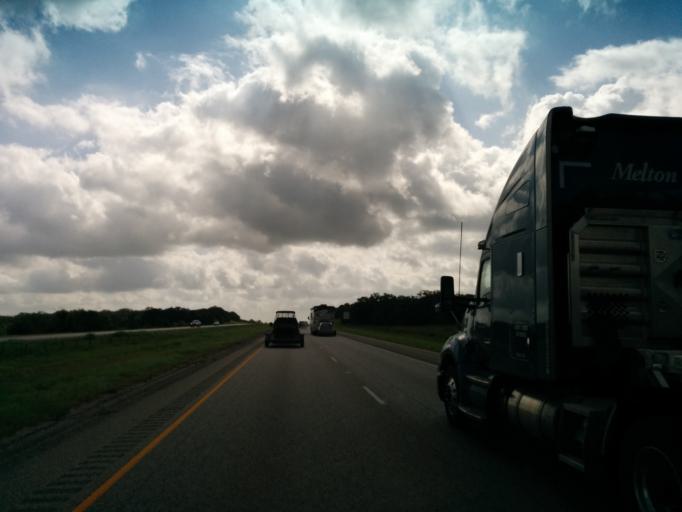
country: US
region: Texas
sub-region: Gonzales County
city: Waelder
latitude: 29.6598
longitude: -97.4024
